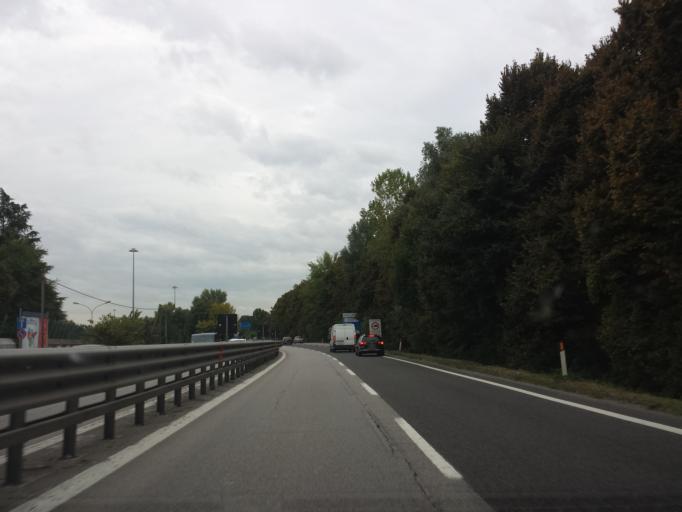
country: IT
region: Veneto
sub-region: Provincia di Padova
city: Padova
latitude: 45.4152
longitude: 11.8531
